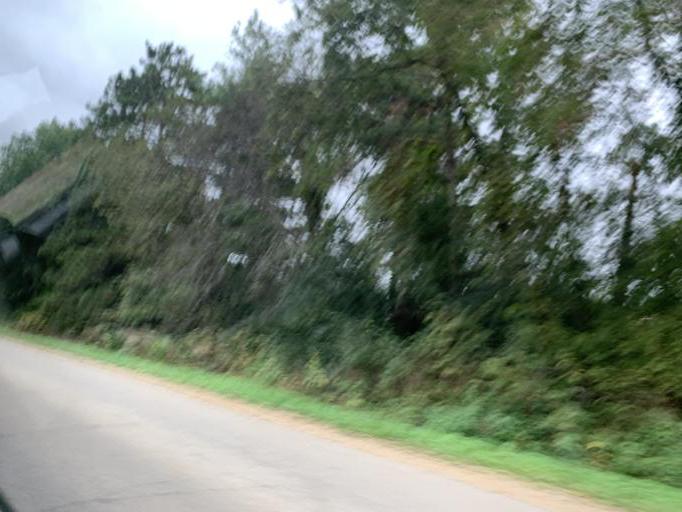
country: US
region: Wisconsin
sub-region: Sauk County
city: Prairie du Sac
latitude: 43.2877
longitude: -89.7788
